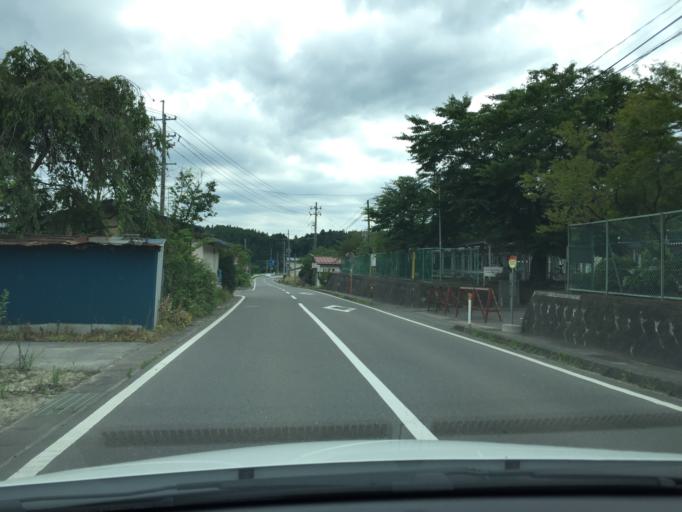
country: JP
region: Fukushima
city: Sukagawa
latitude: 37.3011
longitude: 140.2107
